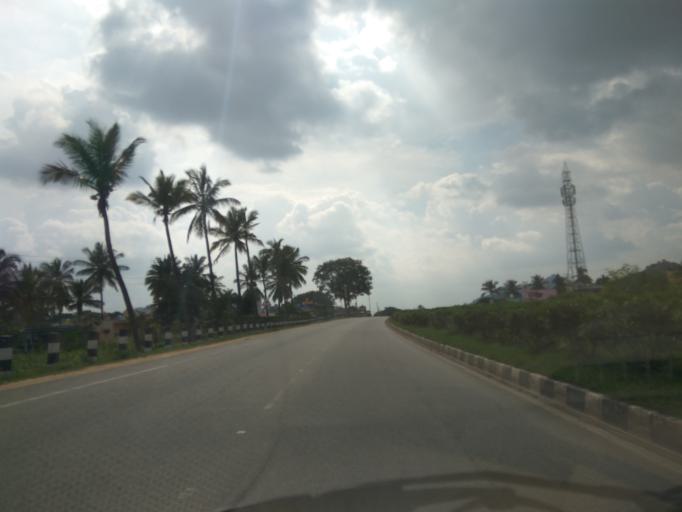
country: IN
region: Karnataka
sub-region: Kolar
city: Kolar
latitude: 13.1188
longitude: 78.0833
